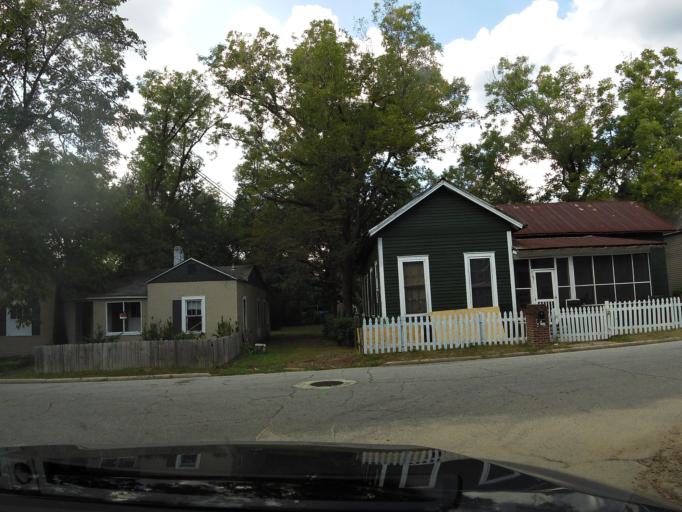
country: US
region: Georgia
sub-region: Lowndes County
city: Valdosta
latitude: 30.8322
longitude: -83.2861
